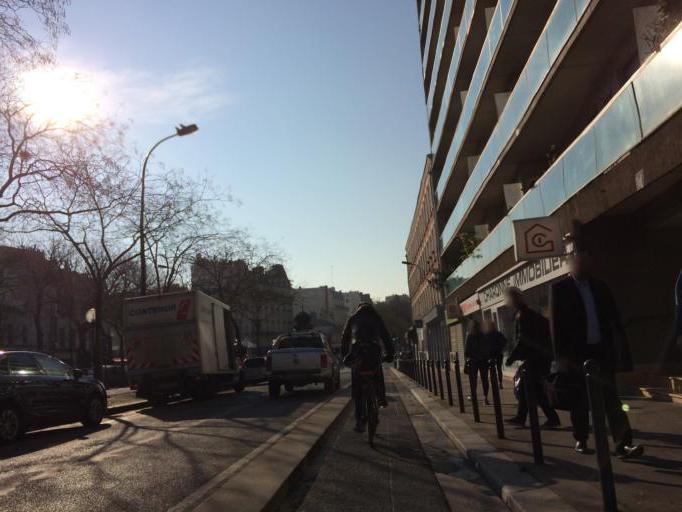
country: FR
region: Ile-de-France
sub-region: Departement du Val-de-Marne
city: Saint-Mande
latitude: 48.8519
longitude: 2.3978
